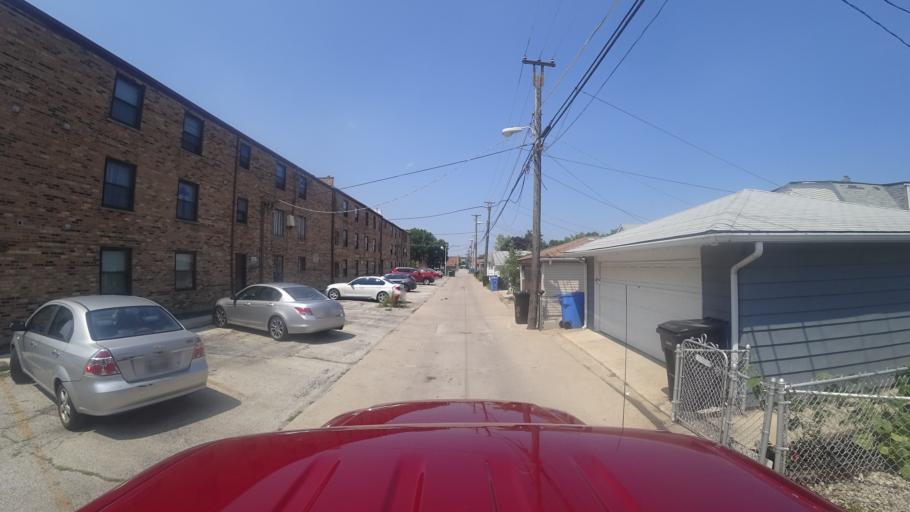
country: US
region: Illinois
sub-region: Cook County
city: Stickney
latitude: 41.7904
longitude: -87.7372
